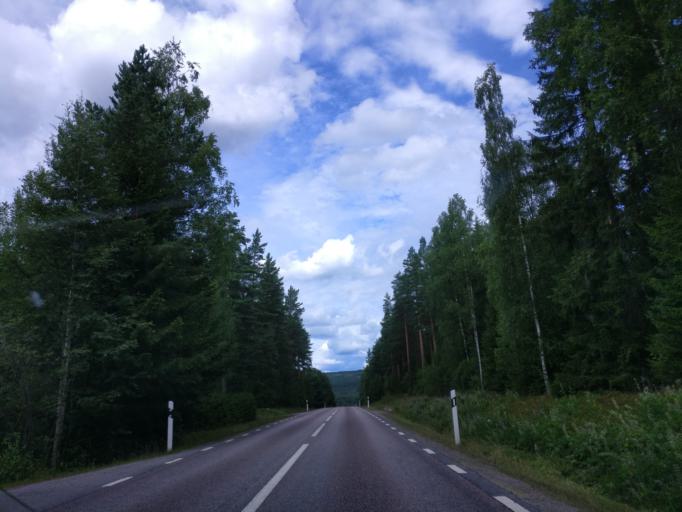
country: SE
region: Vaermland
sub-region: Hagfors Kommun
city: Ekshaerad
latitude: 60.1659
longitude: 13.4116
